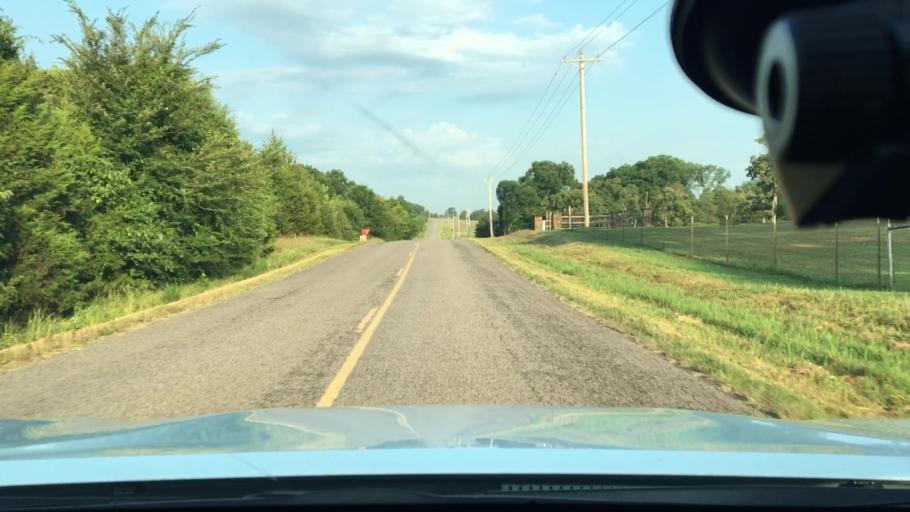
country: US
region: Arkansas
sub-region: Johnson County
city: Coal Hill
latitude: 35.3663
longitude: -93.6083
